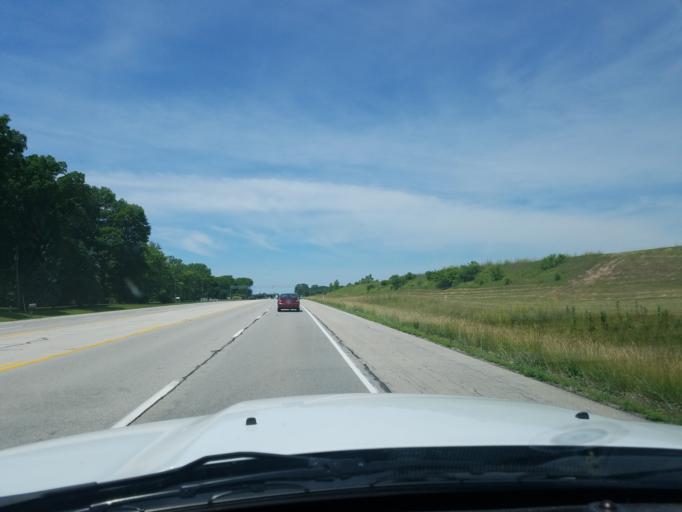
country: US
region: Indiana
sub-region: Delaware County
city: Yorktown
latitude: 40.1136
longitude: -85.4886
